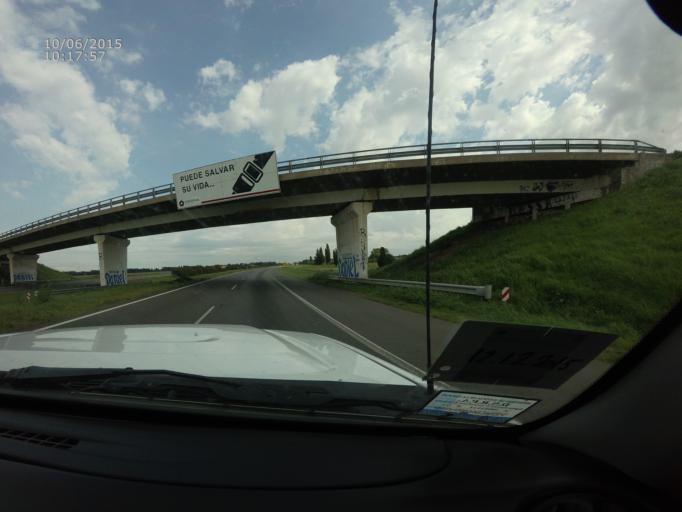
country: AR
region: Buenos Aires
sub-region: Partido de San Pedro
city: San Pedro
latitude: -33.7452
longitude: -59.7805
